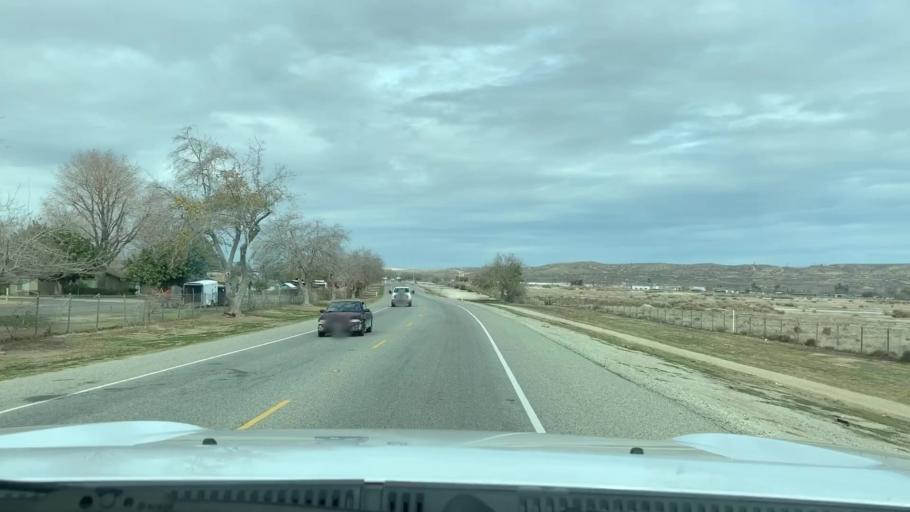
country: US
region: California
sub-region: Kern County
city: Taft
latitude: 35.1443
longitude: -119.4472
